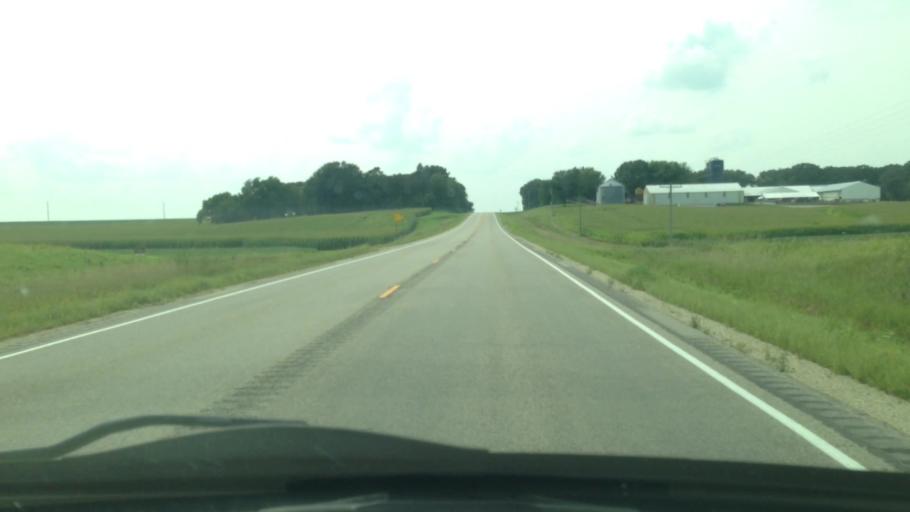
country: US
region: Minnesota
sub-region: Wabasha County
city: Plainview
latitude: 44.1653
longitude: -92.2109
